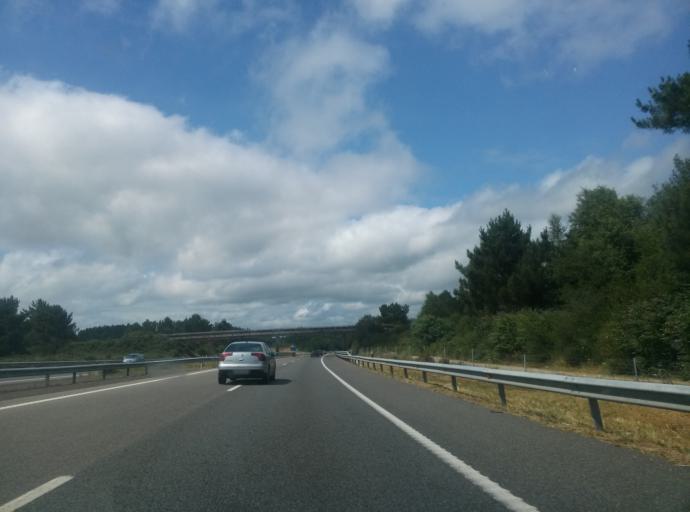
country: ES
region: Galicia
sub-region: Provincia de Lugo
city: Outeiro de Rei
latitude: 43.0677
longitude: -7.5720
